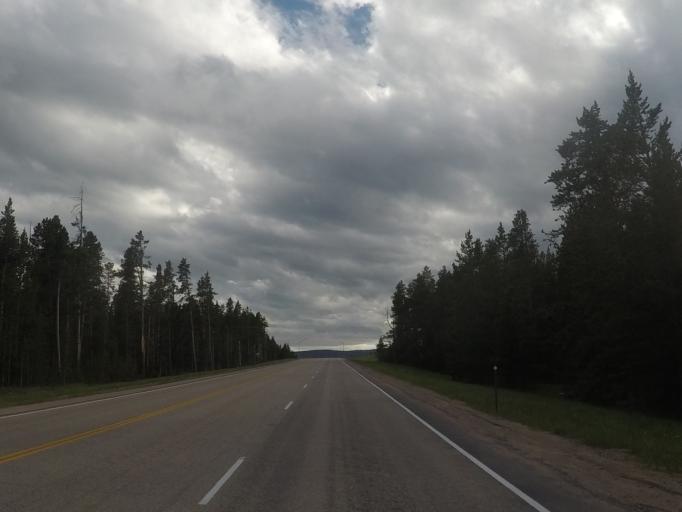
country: US
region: Wyoming
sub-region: Sheridan County
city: Sheridan
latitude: 44.7881
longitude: -107.4928
